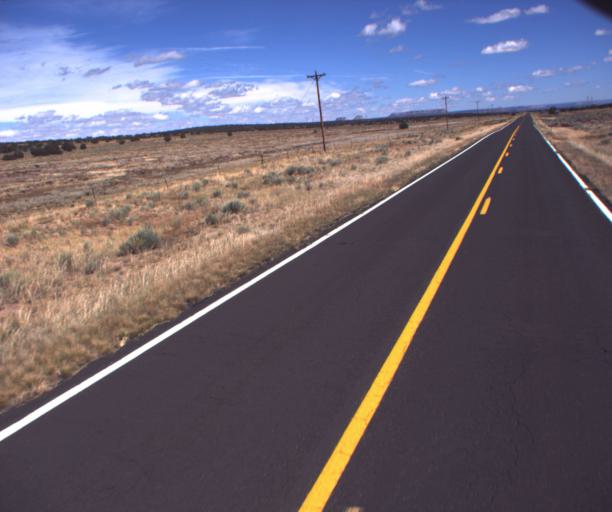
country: US
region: New Mexico
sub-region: McKinley County
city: Zuni Pueblo
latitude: 35.0103
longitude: -109.0697
